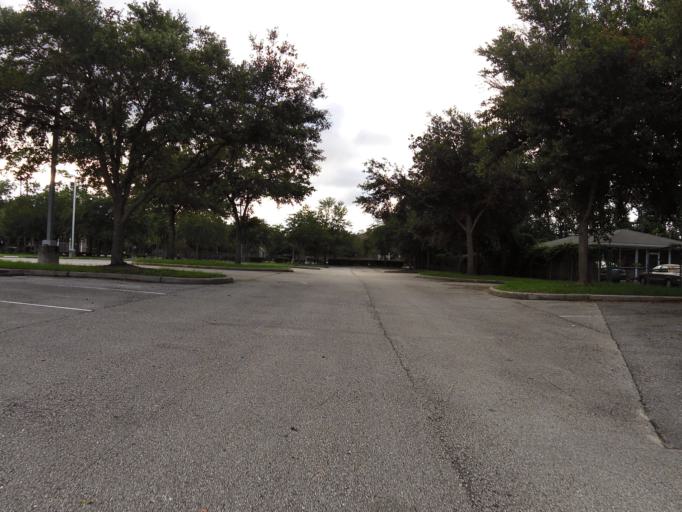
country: US
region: Florida
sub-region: Duval County
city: Jacksonville
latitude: 30.3017
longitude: -81.6175
